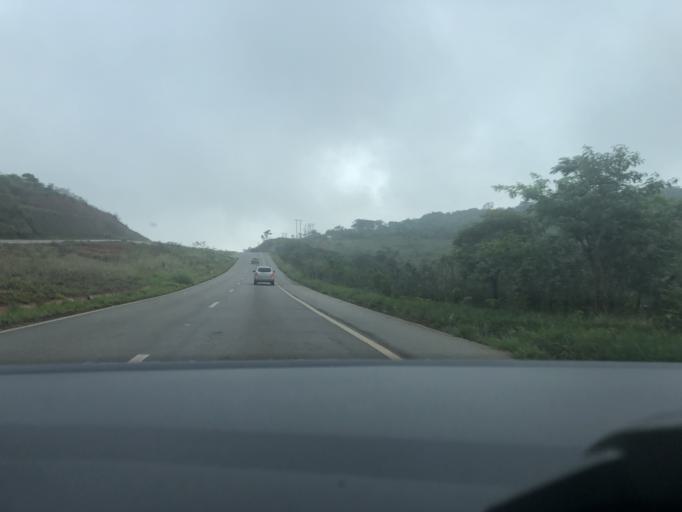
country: BR
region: Minas Gerais
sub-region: Congonhas
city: Congonhas
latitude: -20.5941
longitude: -43.9405
